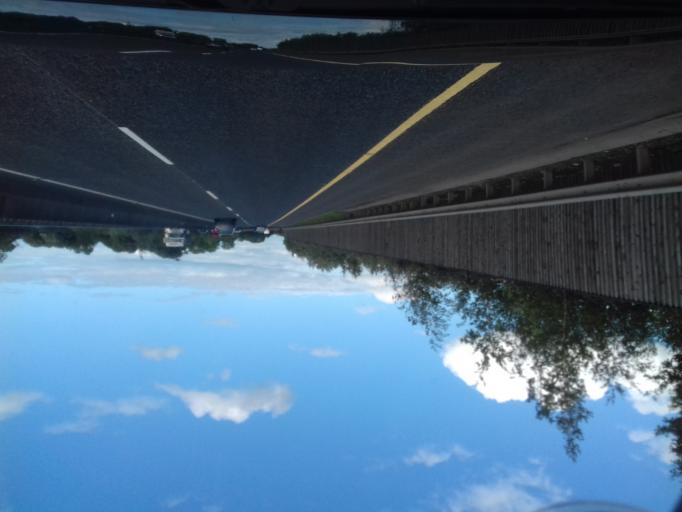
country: IE
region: Leinster
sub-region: An Iarmhi
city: Kilbeggan
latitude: 53.3601
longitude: -7.4282
